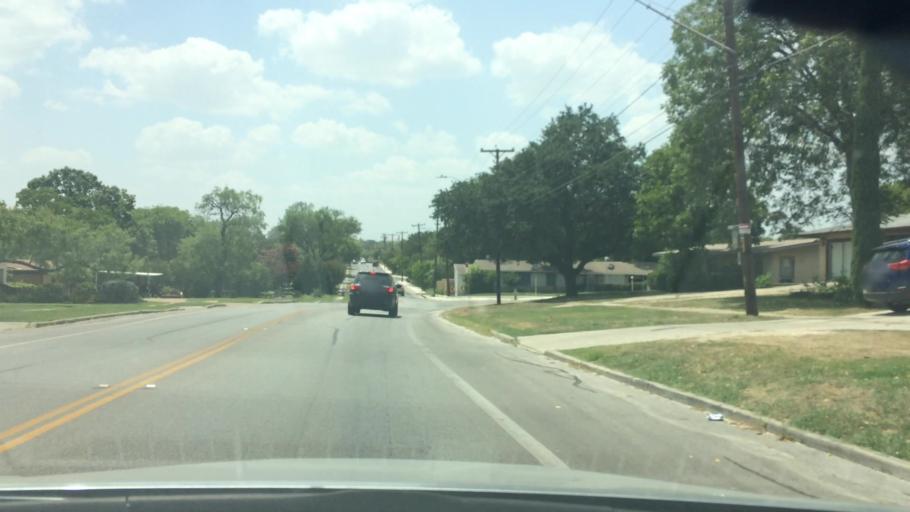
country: US
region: Texas
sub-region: Bexar County
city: Olmos Park
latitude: 29.5043
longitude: -98.4883
